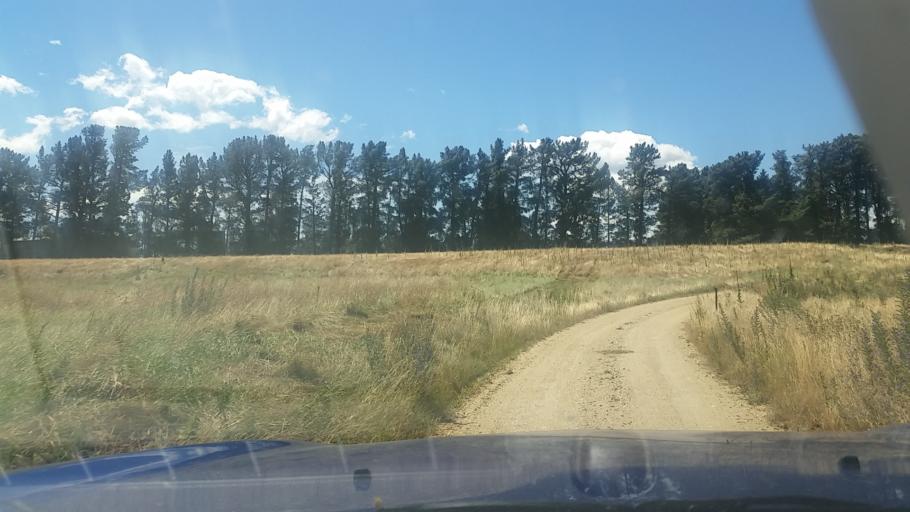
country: NZ
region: Otago
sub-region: Queenstown-Lakes District
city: Wanaka
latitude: -45.1500
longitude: 169.3986
